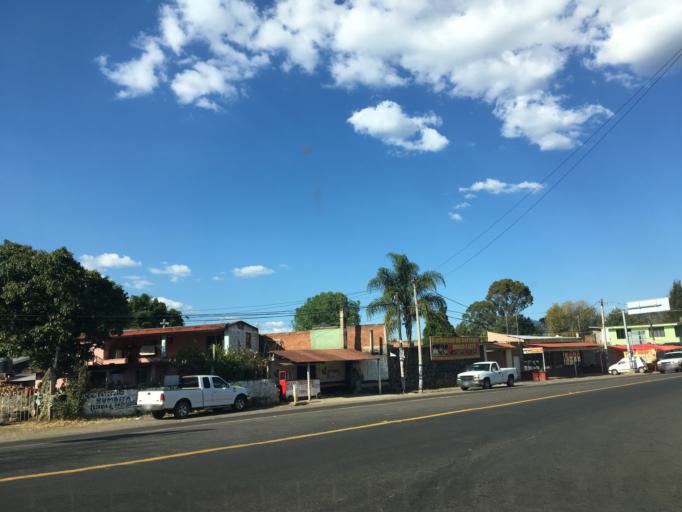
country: MX
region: Michoacan
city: Patzcuaro
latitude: 19.5448
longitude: -101.5864
